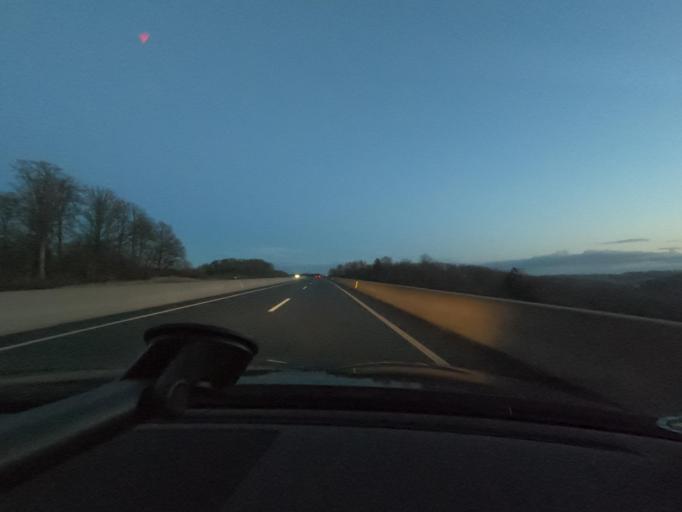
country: DE
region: Lower Saxony
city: Bad Lauterberg im Harz
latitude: 51.6146
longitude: 10.4444
